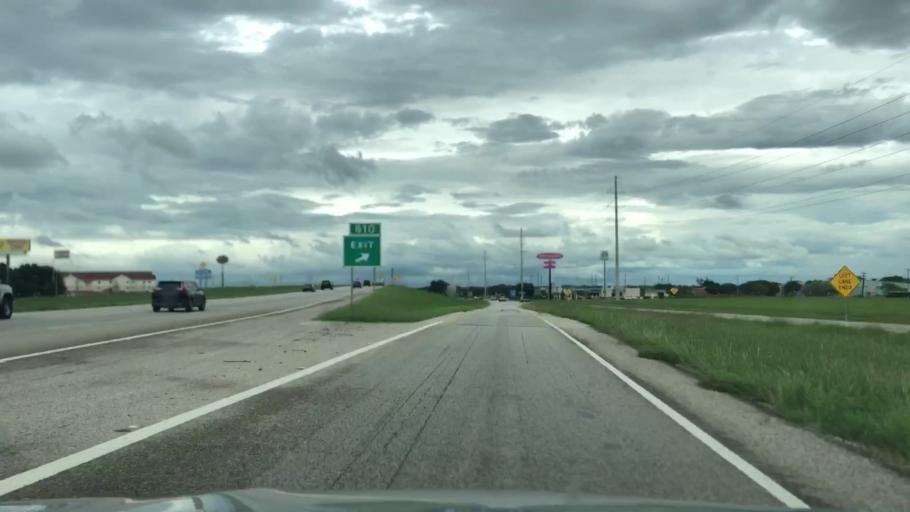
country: US
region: Texas
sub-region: Guadalupe County
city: Seguin
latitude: 29.5991
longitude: -97.9552
